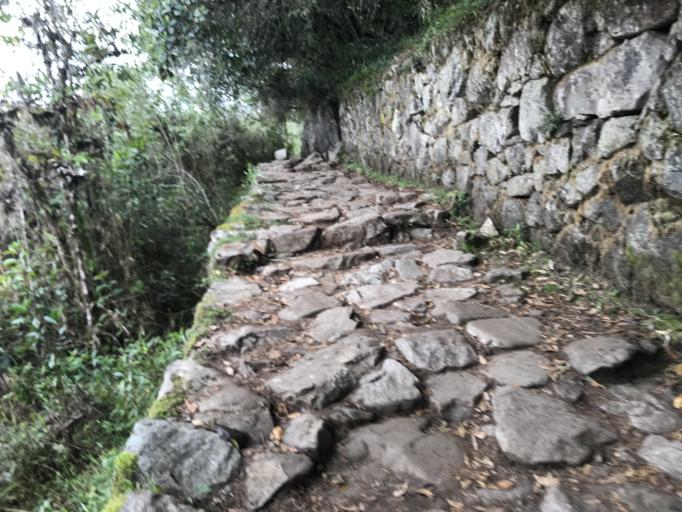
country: PE
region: Cusco
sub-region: Provincia de La Convencion
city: Santa Teresa
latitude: -13.1705
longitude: -72.5379
